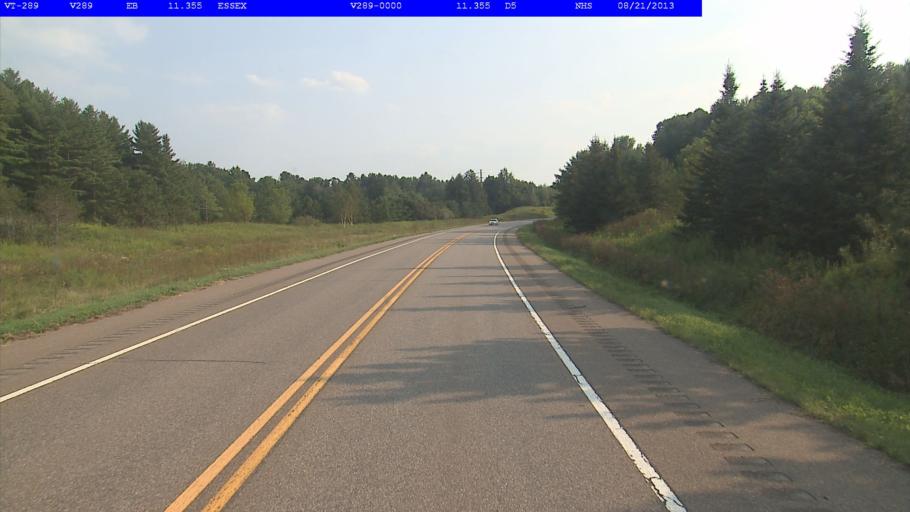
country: US
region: Vermont
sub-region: Chittenden County
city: Essex Junction
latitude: 44.4888
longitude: -73.0636
